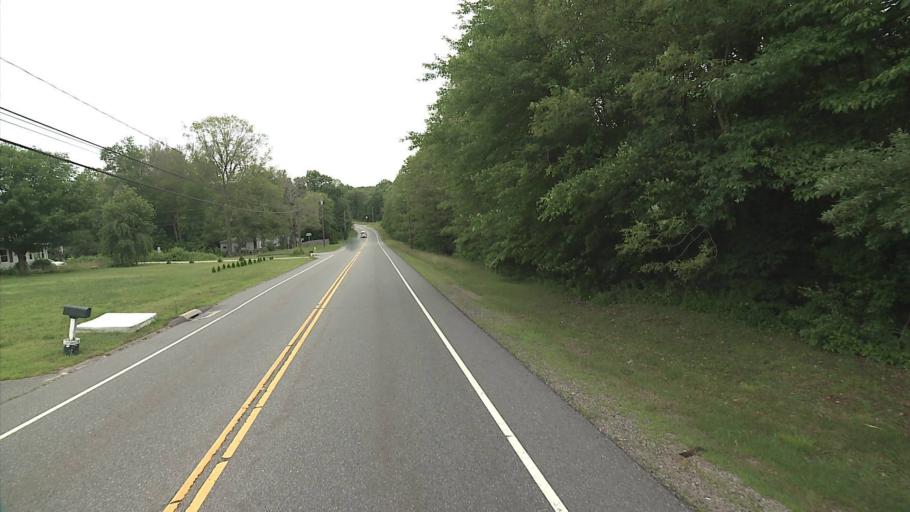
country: US
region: Connecticut
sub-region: New London County
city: Ledyard Center
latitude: 41.4183
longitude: -72.0178
